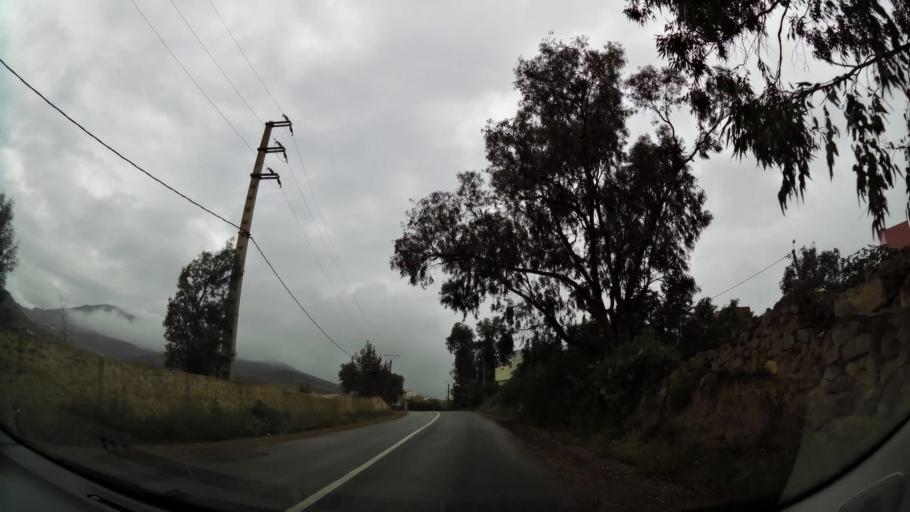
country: MA
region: Oriental
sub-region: Nador
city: Nador
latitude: 35.1426
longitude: -3.0453
